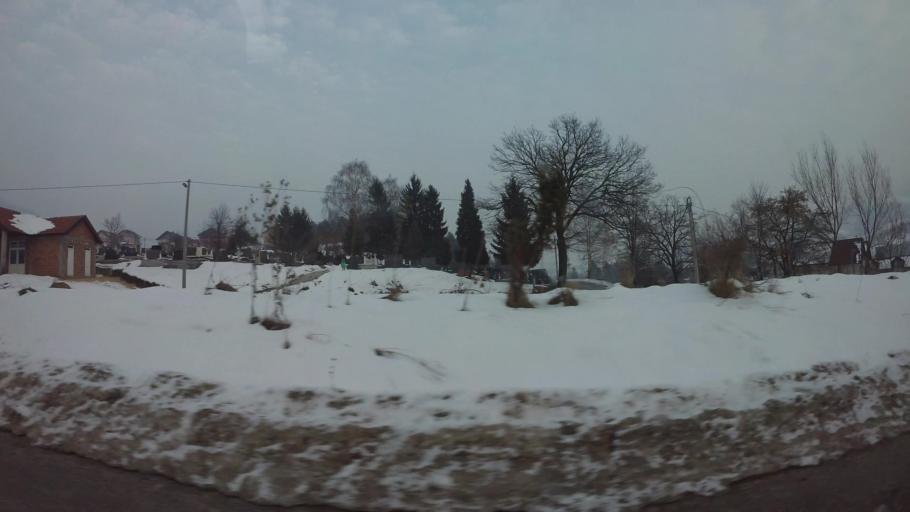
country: BA
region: Federation of Bosnia and Herzegovina
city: Vogosca
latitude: 43.9010
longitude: 18.3550
